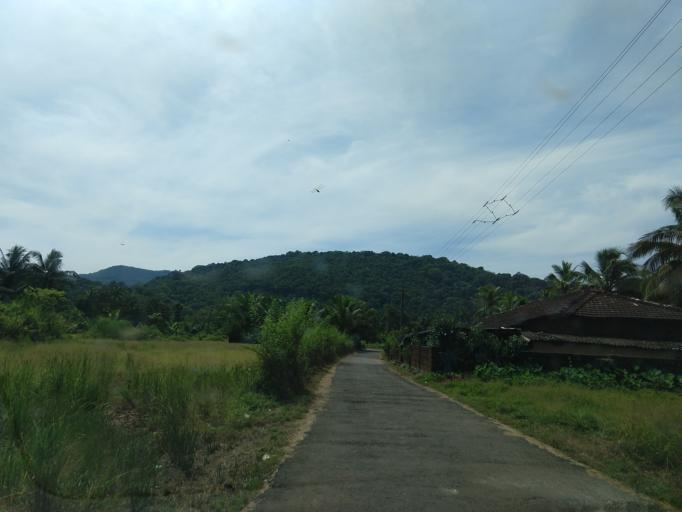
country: IN
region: Maharashtra
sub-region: Sindhudurg
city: Savantvadi
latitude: 15.9761
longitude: 73.7869
